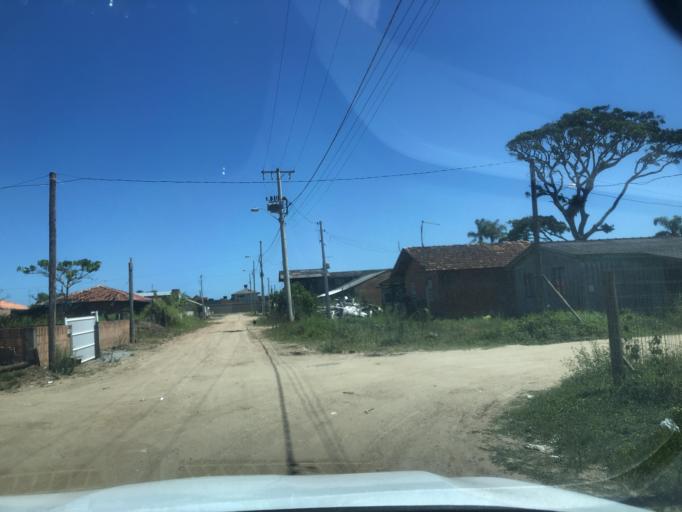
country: BR
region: Santa Catarina
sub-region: Sao Francisco Do Sul
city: Sao Francisco do Sul
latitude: -26.2304
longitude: -48.5223
